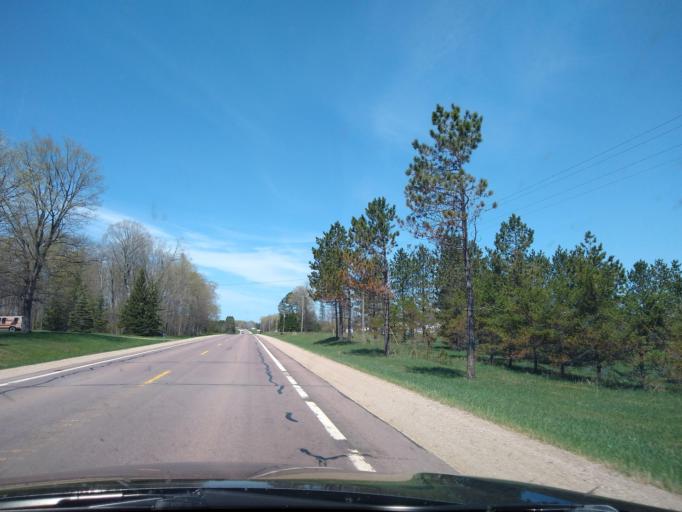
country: US
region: Michigan
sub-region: Marquette County
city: K. I. Sawyer Air Force Base
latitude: 46.2441
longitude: -87.0787
